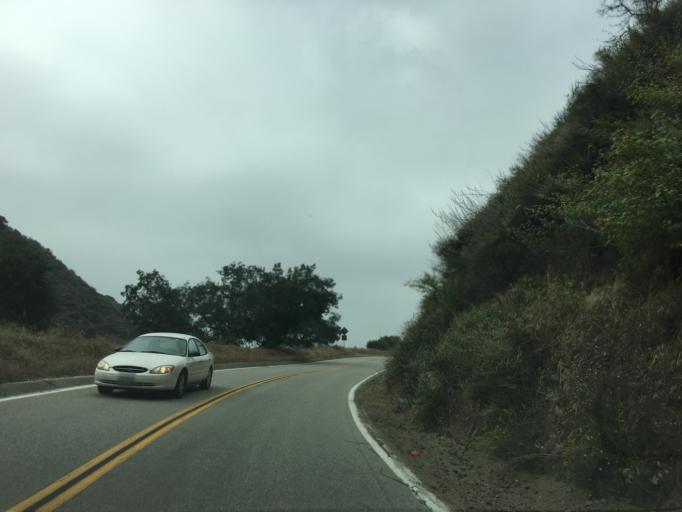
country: US
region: California
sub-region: Los Angeles County
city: Glendora
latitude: 34.1668
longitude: -117.8390
